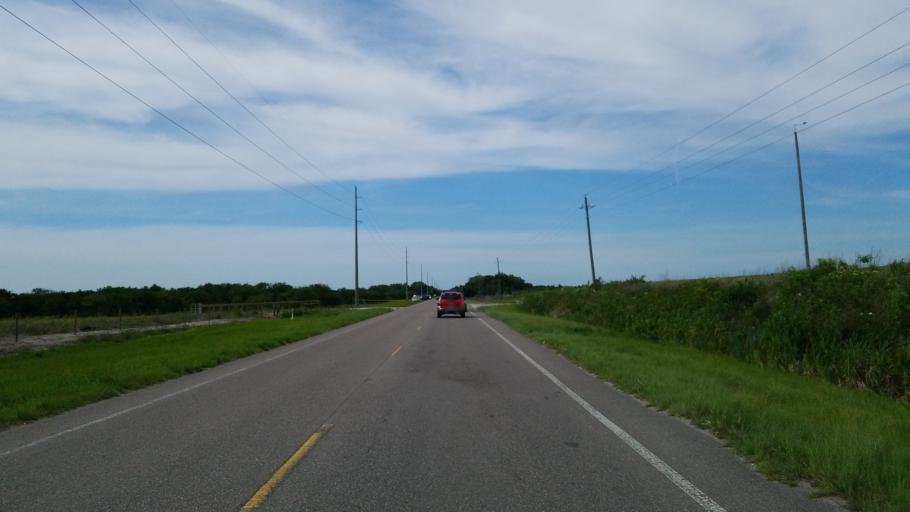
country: US
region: Florida
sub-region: Hillsborough County
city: Balm
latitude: 27.6668
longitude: -82.1462
